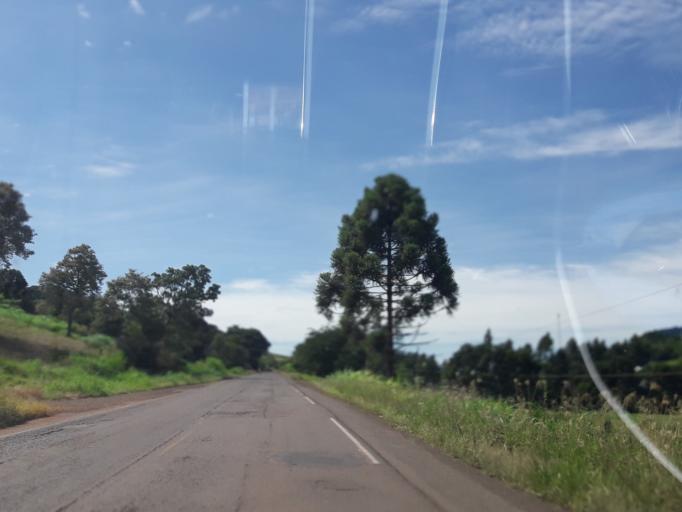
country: AR
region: Misiones
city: Bernardo de Irigoyen
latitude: -26.3708
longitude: -53.5322
